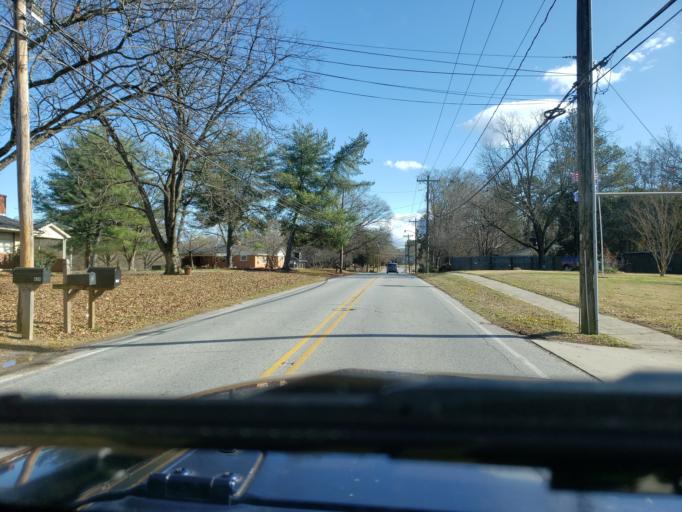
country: US
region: North Carolina
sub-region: Cleveland County
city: White Plains
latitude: 35.1763
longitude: -81.4520
